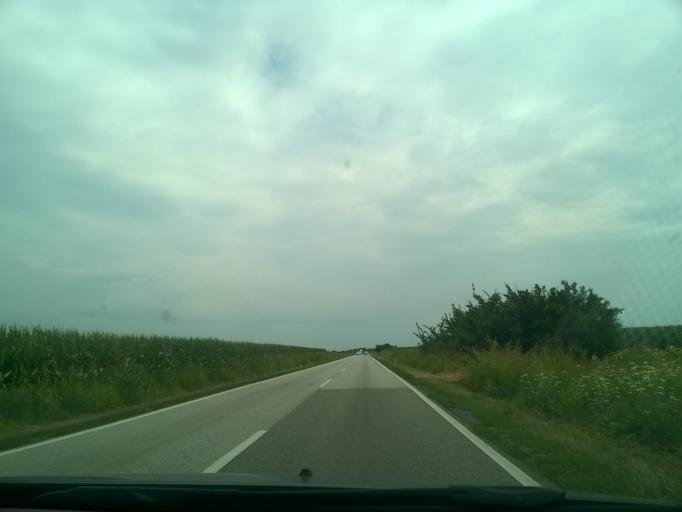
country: RS
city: Sutjeska
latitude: 45.3813
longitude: 20.7131
